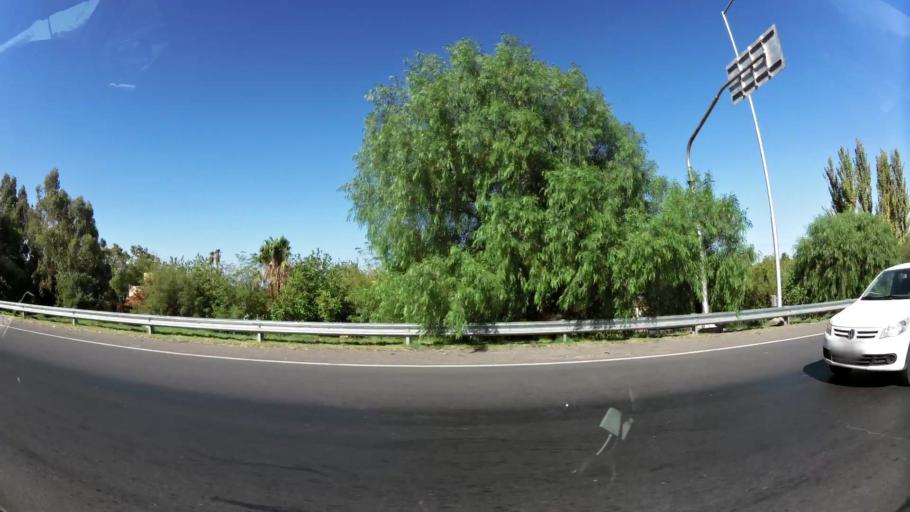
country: AR
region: San Juan
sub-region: Departamento de Santa Lucia
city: Santa Lucia
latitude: -31.5371
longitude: -68.5038
